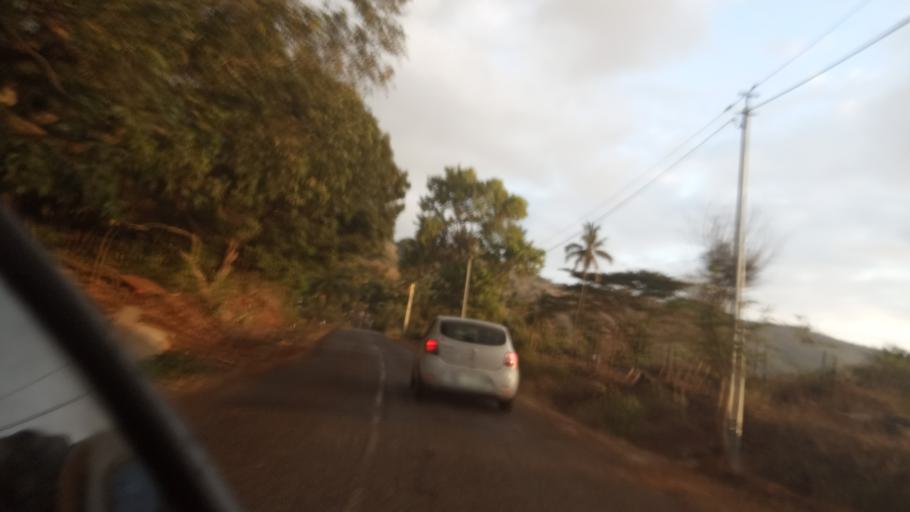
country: YT
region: Kani-Keli
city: Kani Keli
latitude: -12.9378
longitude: 45.1020
